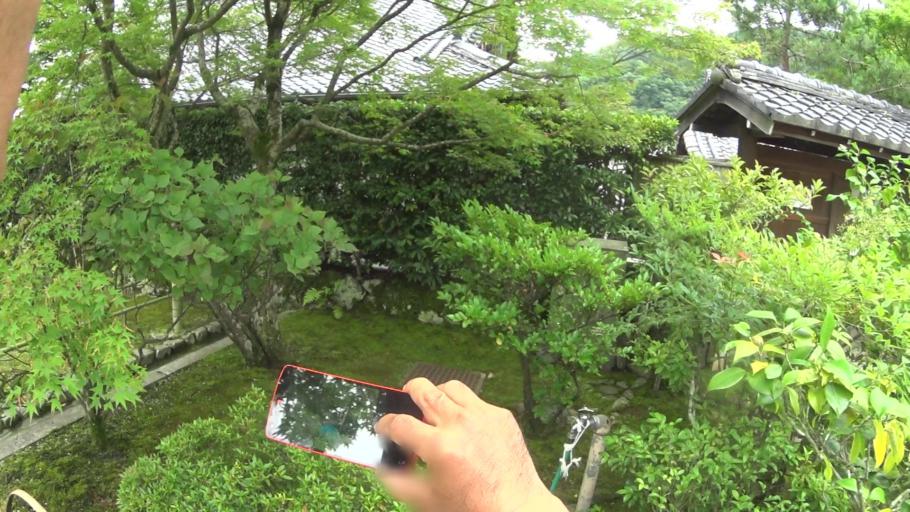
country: JP
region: Kyoto
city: Muko
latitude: 35.0154
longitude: 135.6733
